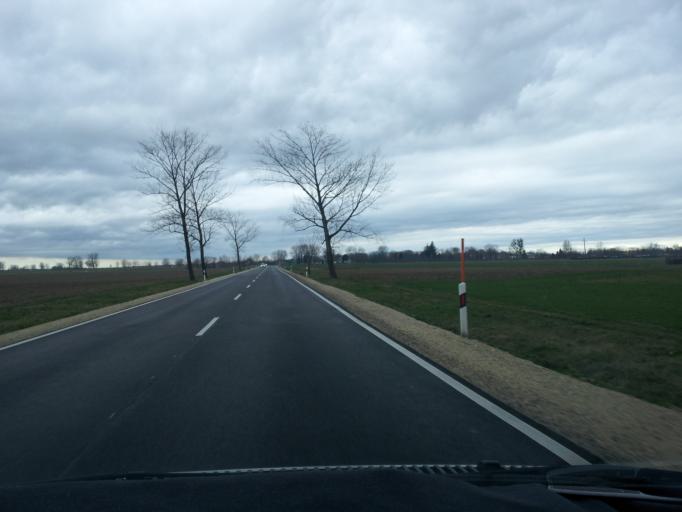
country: HU
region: Gyor-Moson-Sopron
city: Beled
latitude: 47.4590
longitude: 17.1002
